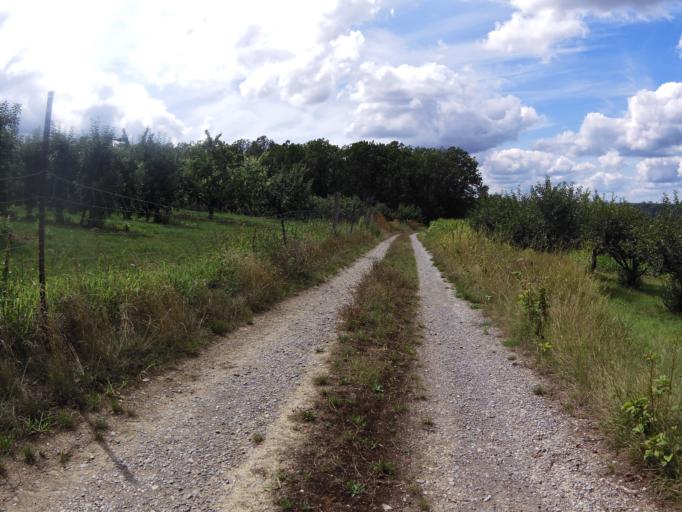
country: DE
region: Bavaria
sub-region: Regierungsbezirk Unterfranken
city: Sommerhausen
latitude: 49.7079
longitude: 10.0343
